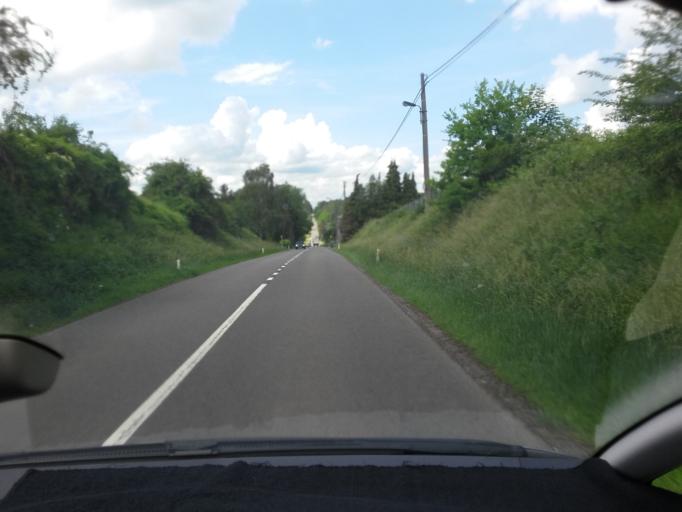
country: BE
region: Wallonia
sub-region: Province de Namur
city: Rochefort
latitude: 50.1268
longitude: 5.2413
